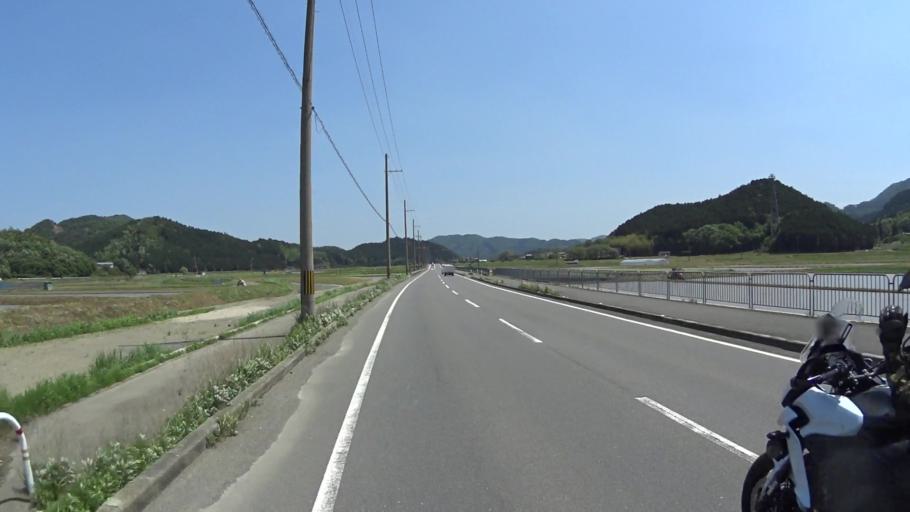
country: JP
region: Kyoto
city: Kameoka
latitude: 35.0483
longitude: 135.4772
